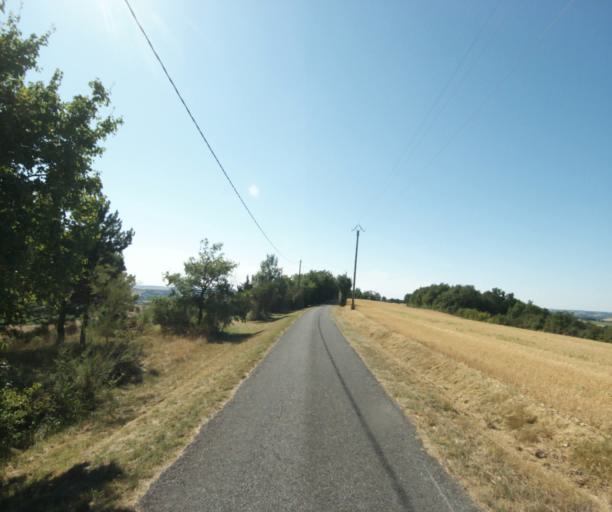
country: FR
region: Midi-Pyrenees
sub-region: Departement de la Haute-Garonne
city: Saint-Felix-Lauragais
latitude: 43.5152
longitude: 1.9251
